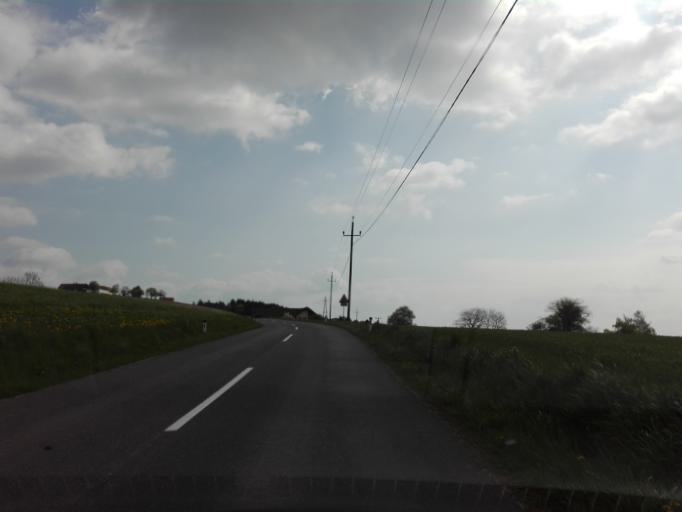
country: AT
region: Upper Austria
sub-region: Politischer Bezirk Perg
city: Perg
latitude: 48.2765
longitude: 14.6649
